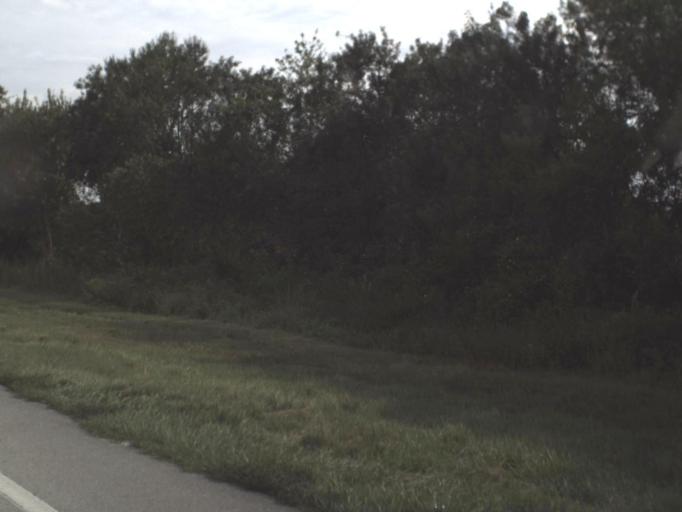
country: US
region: Florida
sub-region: Okeechobee County
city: Taylor Creek
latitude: 27.2053
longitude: -80.7474
